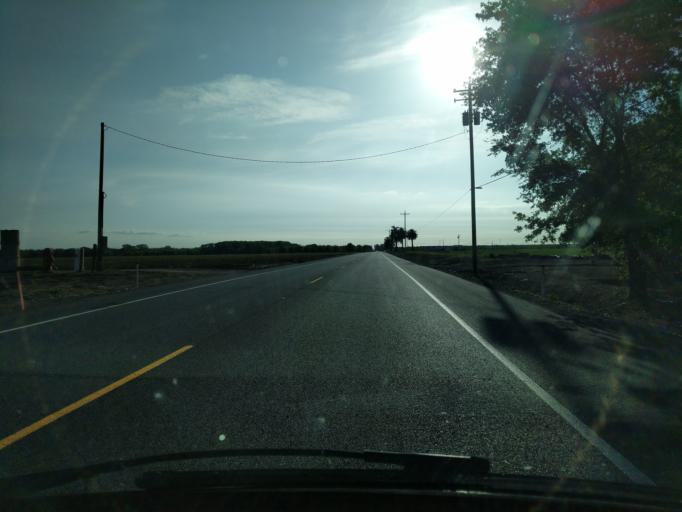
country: US
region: California
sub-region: San Joaquin County
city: Linden
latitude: 37.9298
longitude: -121.0213
